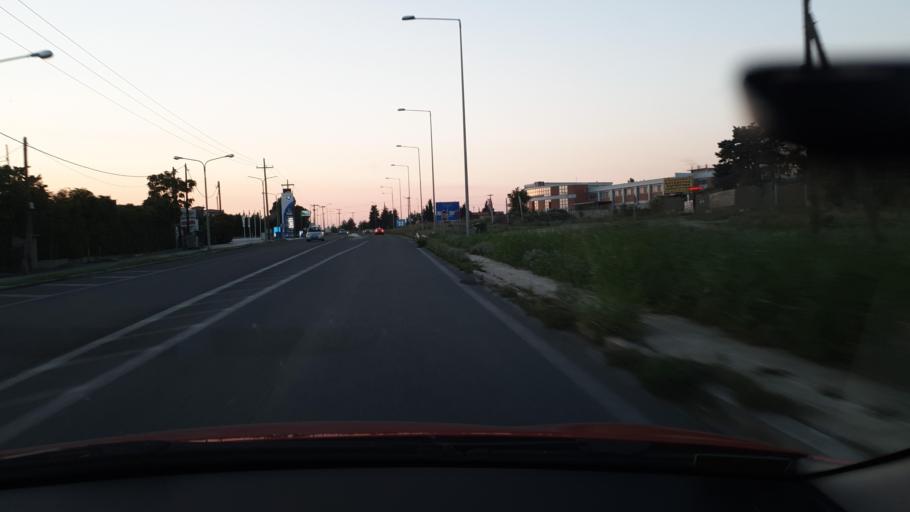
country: GR
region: Central Macedonia
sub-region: Nomos Thessalonikis
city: Thermi
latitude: 40.5312
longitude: 23.0414
